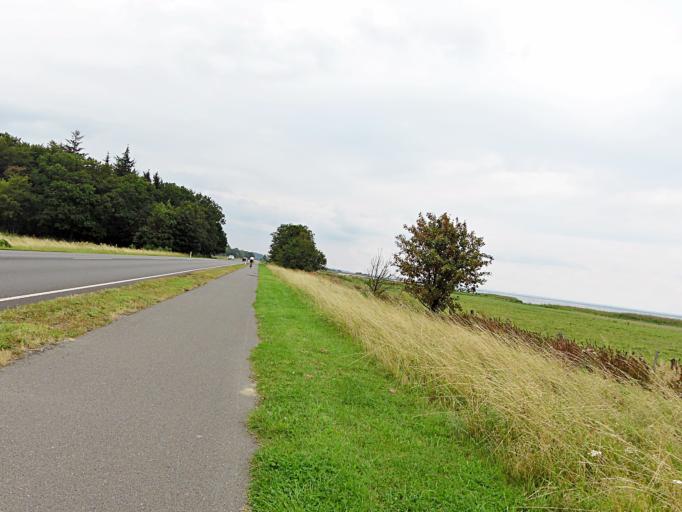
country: DK
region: Capital Region
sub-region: Fredensborg Kommune
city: Niva
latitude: 55.9211
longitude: 12.5155
